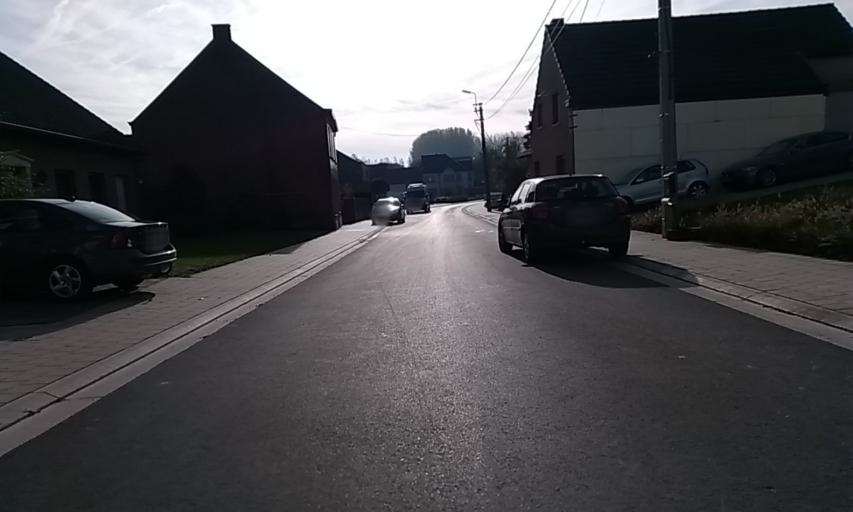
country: BE
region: Flanders
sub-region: Provincie Oost-Vlaanderen
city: Sint-Lievens-Houtem
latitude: 50.9245
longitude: 3.8939
